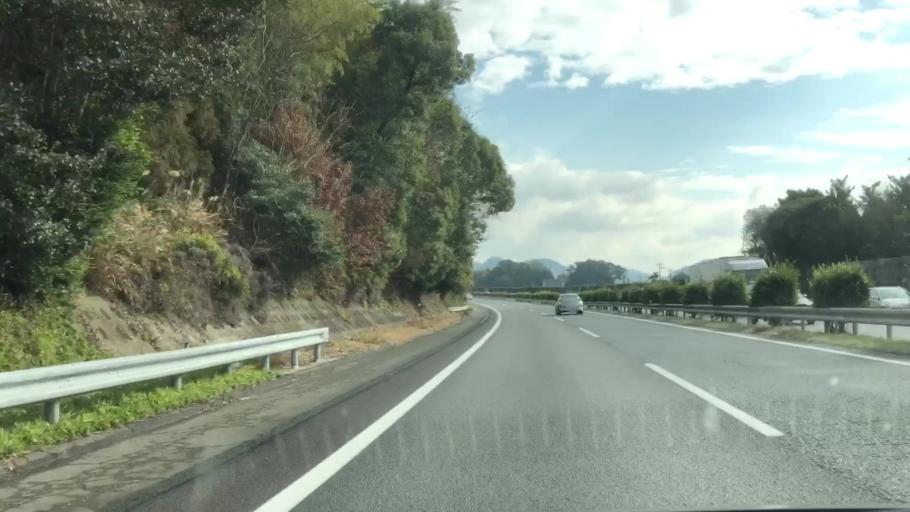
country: JP
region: Fukuoka
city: Setakamachi-takayanagi
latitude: 33.1220
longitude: 130.5204
